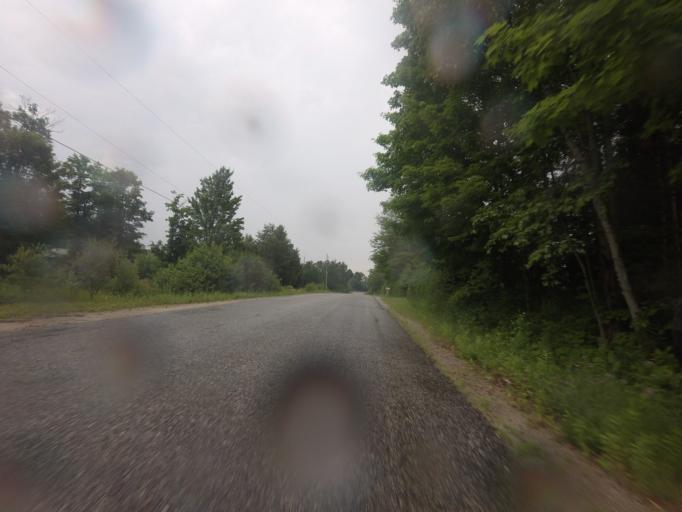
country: CA
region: Quebec
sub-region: Outaouais
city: Maniwaki
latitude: 46.4289
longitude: -75.9500
